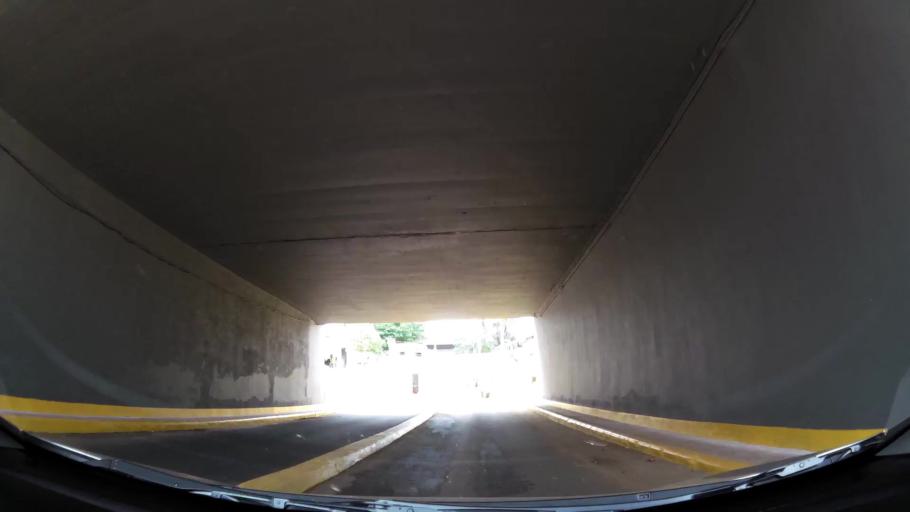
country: PY
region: Alto Parana
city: Ciudad del Este
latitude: -25.5096
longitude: -54.6071
